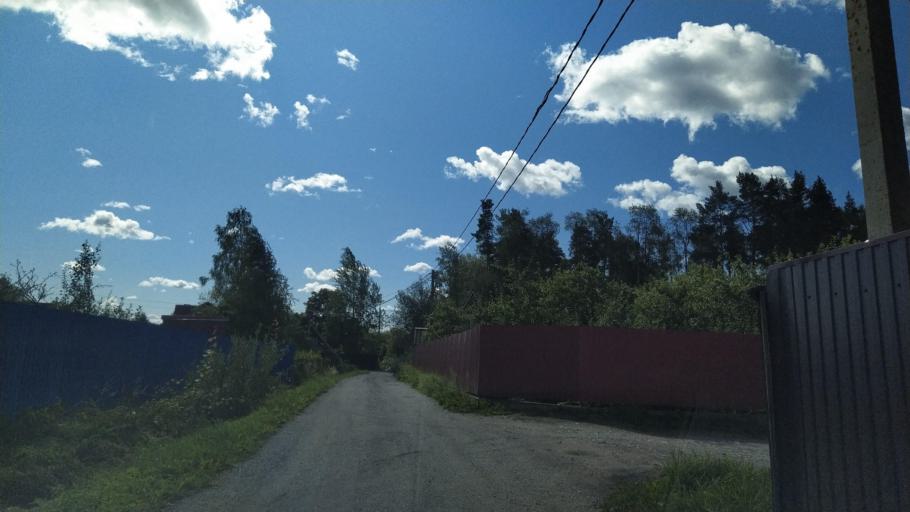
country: RU
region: Leningrad
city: Priozersk
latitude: 61.0032
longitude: 30.1744
